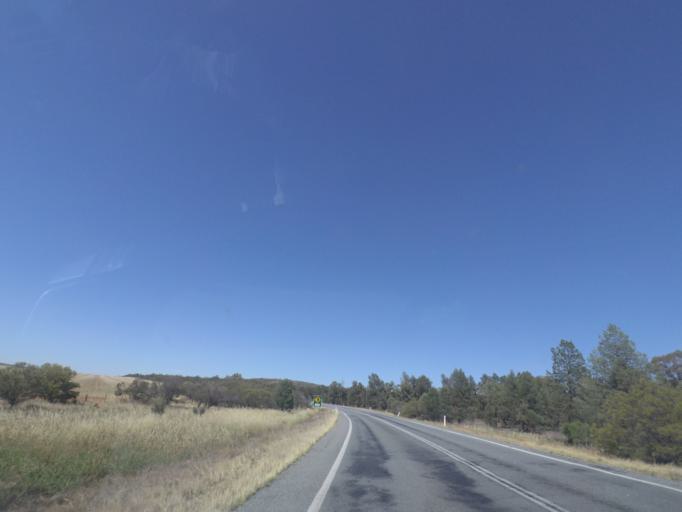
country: AU
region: New South Wales
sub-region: Narrandera
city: Narrandera
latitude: -34.4198
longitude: 146.8468
